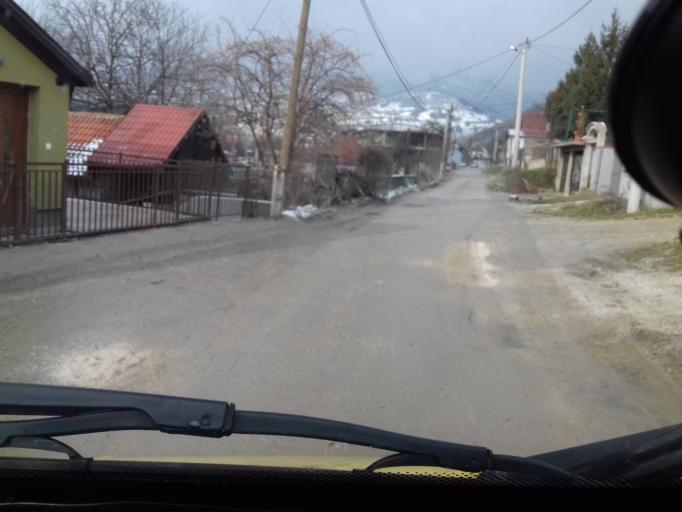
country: BA
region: Federation of Bosnia and Herzegovina
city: Zenica
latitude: 44.2281
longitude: 17.9105
